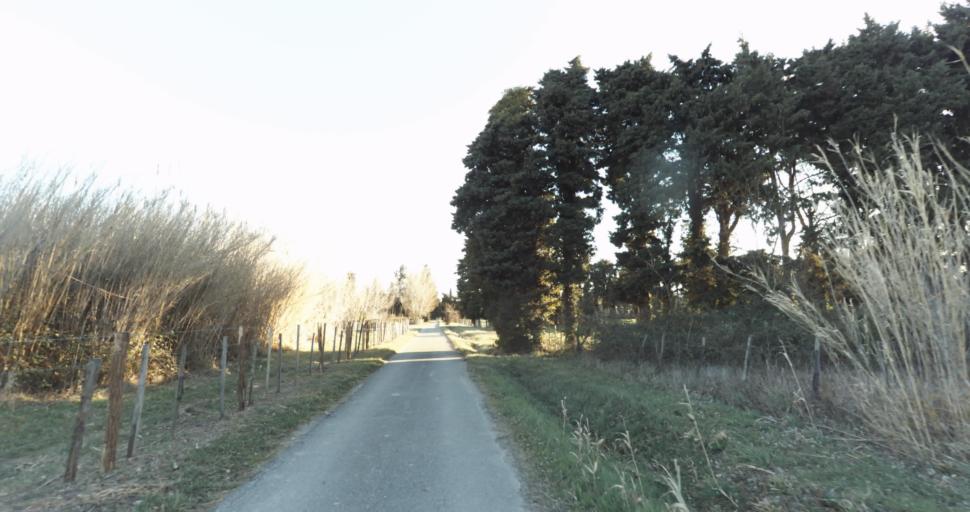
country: FR
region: Provence-Alpes-Cote d'Azur
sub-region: Departement des Bouches-du-Rhone
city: Barbentane
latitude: 43.9165
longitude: 4.7679
